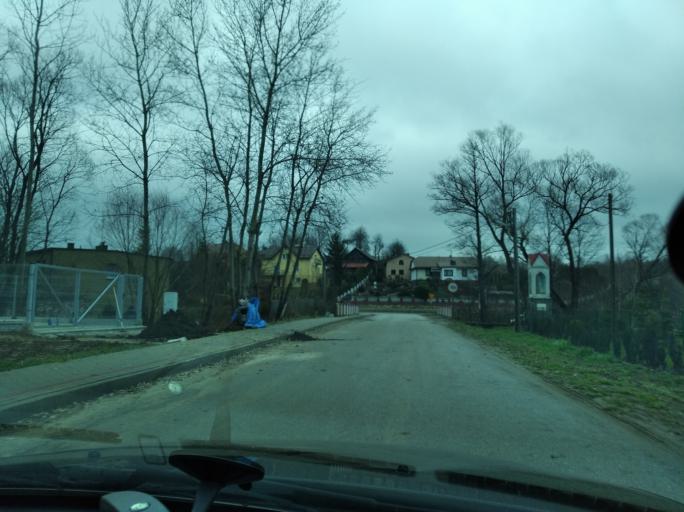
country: PL
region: Subcarpathian Voivodeship
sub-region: Powiat przeworski
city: Jawornik Polski
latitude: 49.9105
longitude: 22.2984
